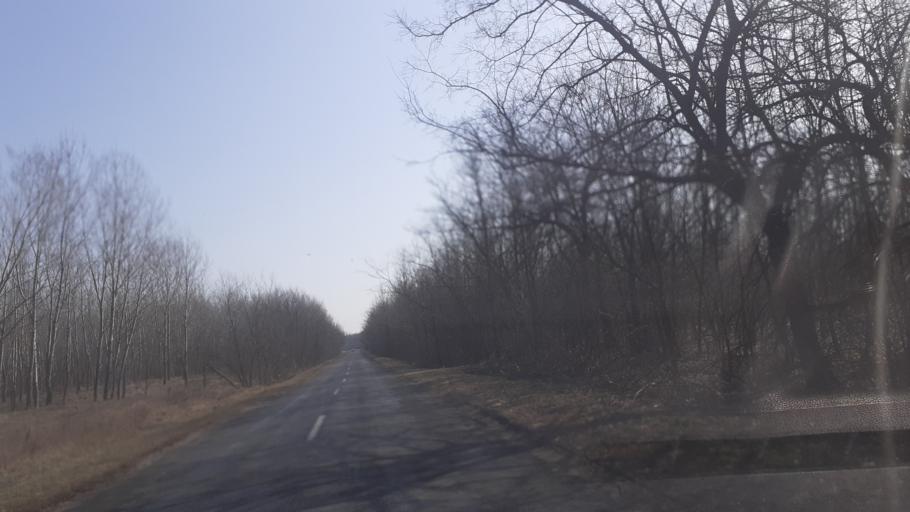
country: HU
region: Pest
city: Orkeny
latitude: 47.0570
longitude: 19.4098
